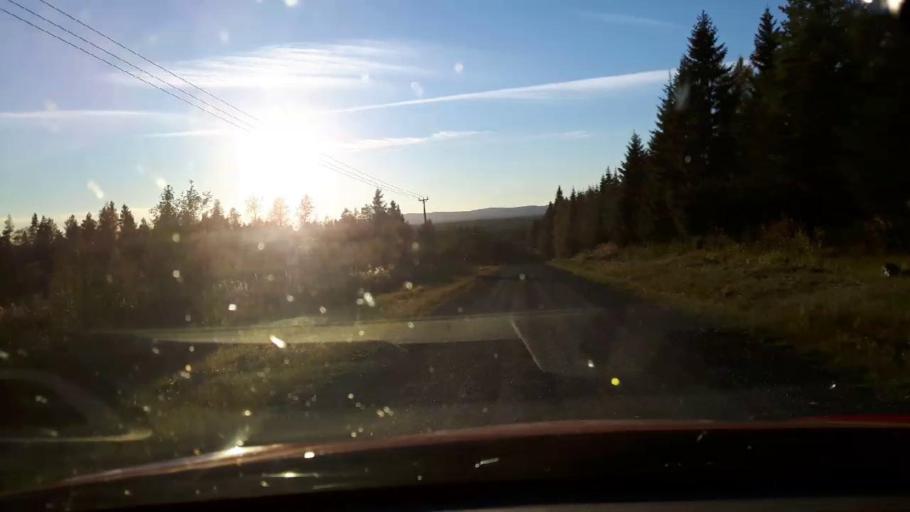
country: SE
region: Jaemtland
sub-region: Krokoms Kommun
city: Krokom
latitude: 63.4524
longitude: 14.5438
